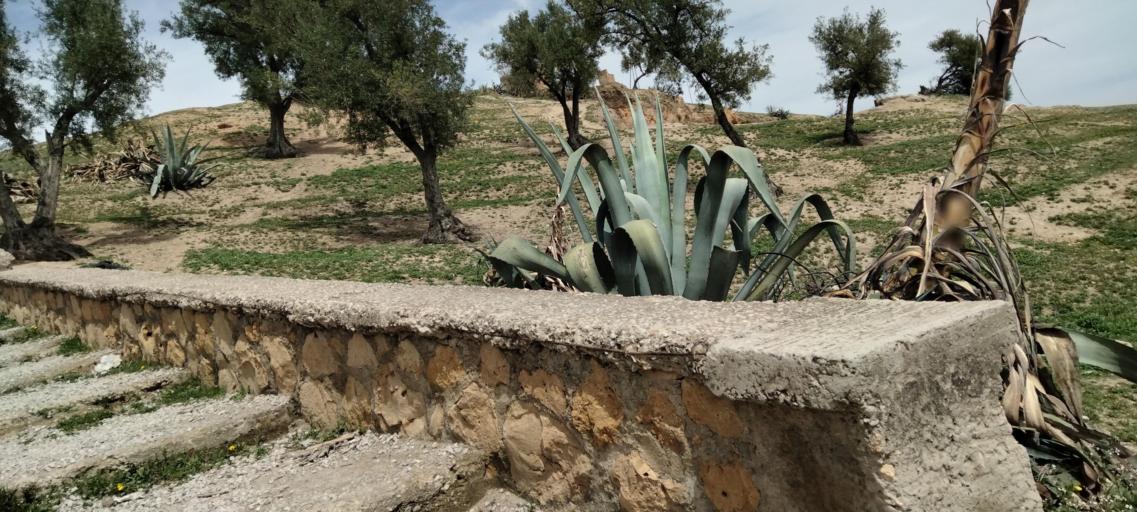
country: MA
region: Fes-Boulemane
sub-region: Fes
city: Fes
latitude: 34.0689
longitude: -4.9809
